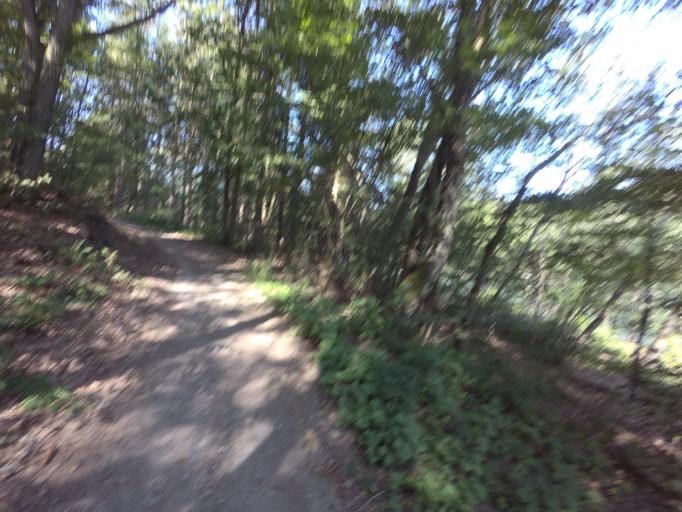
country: DE
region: North Rhine-Westphalia
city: Heimbach
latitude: 50.6067
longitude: 6.3972
